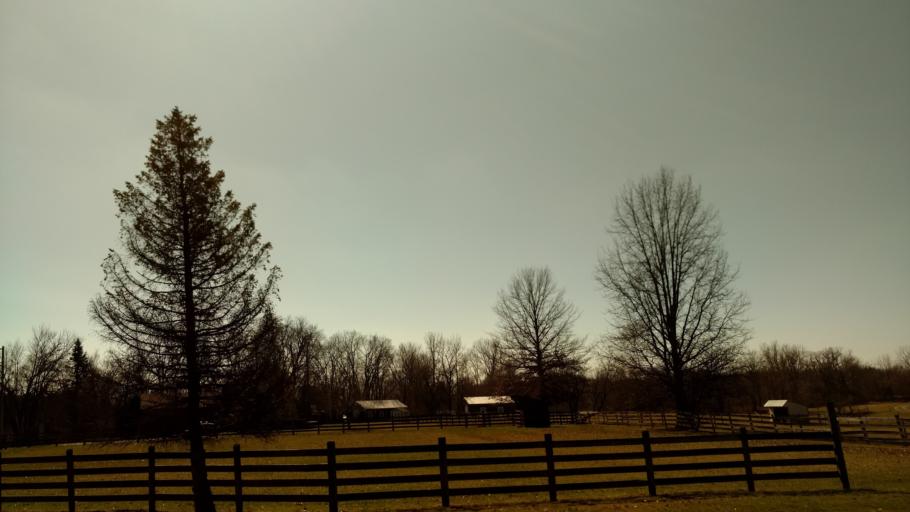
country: US
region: Ohio
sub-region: Morrow County
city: Cardington
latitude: 40.4990
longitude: -82.9232
